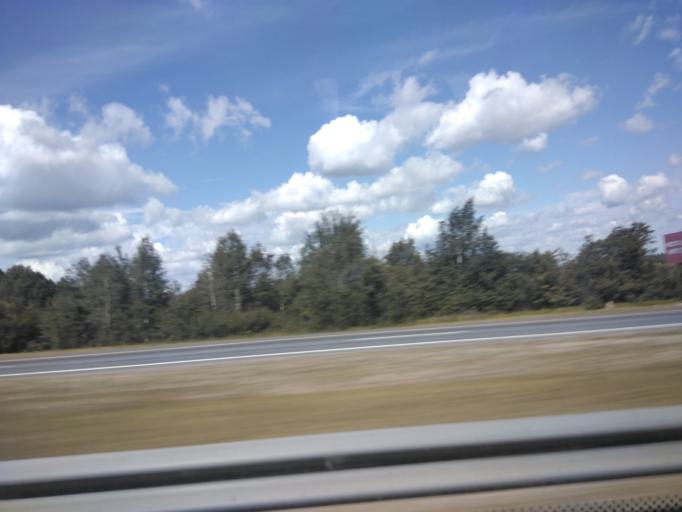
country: RU
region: Moskovskaya
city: Serpukhov
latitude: 54.8479
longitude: 37.4671
